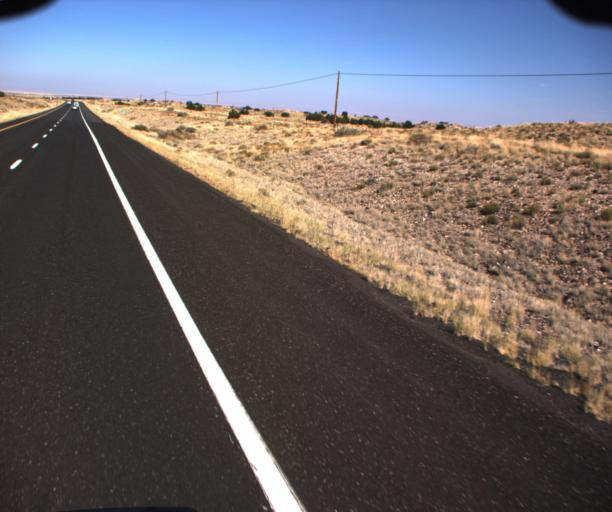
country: US
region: Arizona
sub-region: Coconino County
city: Flagstaff
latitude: 35.5104
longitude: -111.5465
